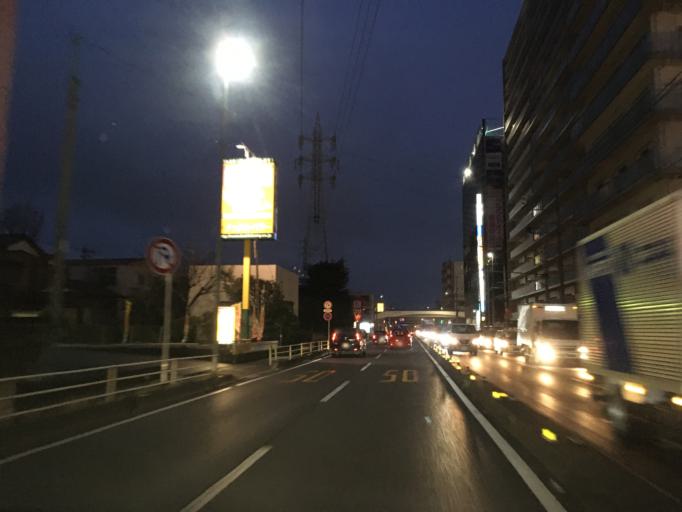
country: JP
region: Saitama
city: Shiki
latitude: 35.8020
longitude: 139.5573
